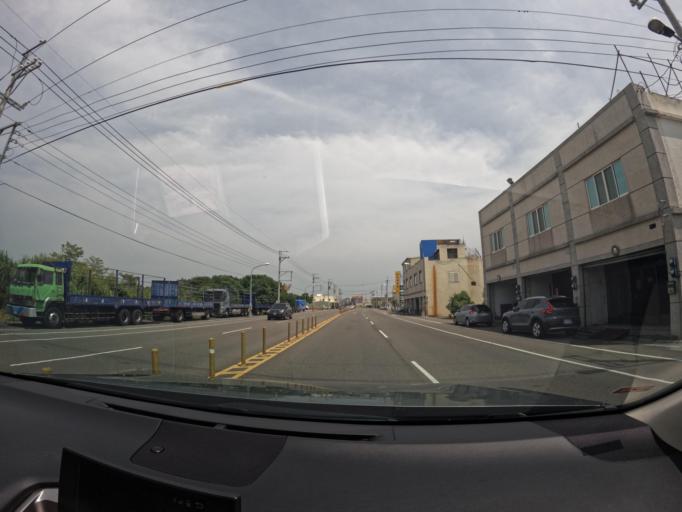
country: TW
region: Taiwan
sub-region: Changhua
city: Chang-hua
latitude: 23.9587
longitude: 120.4582
